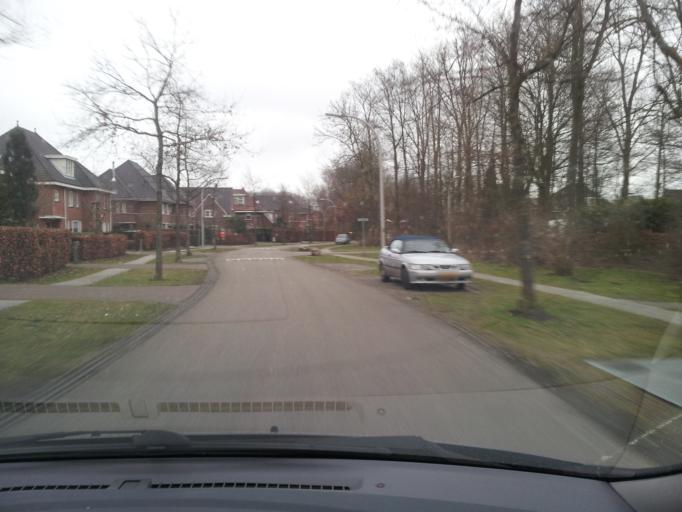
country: NL
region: South Holland
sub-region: Gemeente Den Haag
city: Ypenburg
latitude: 52.0506
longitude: 4.3673
